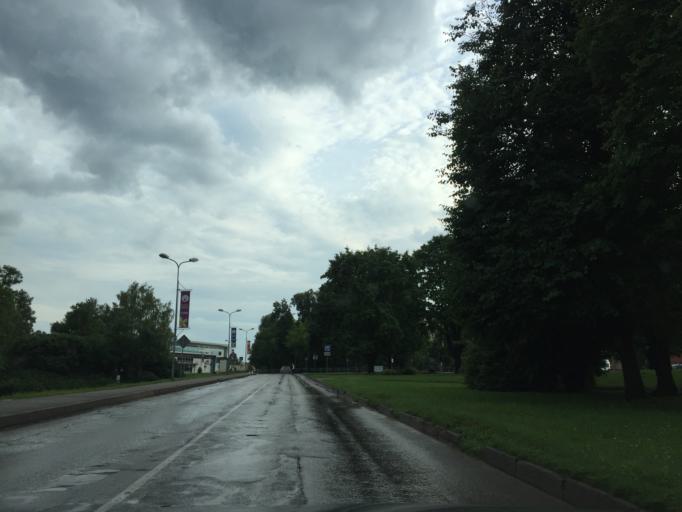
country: LV
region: Dobeles Rajons
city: Dobele
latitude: 56.6233
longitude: 23.2722
